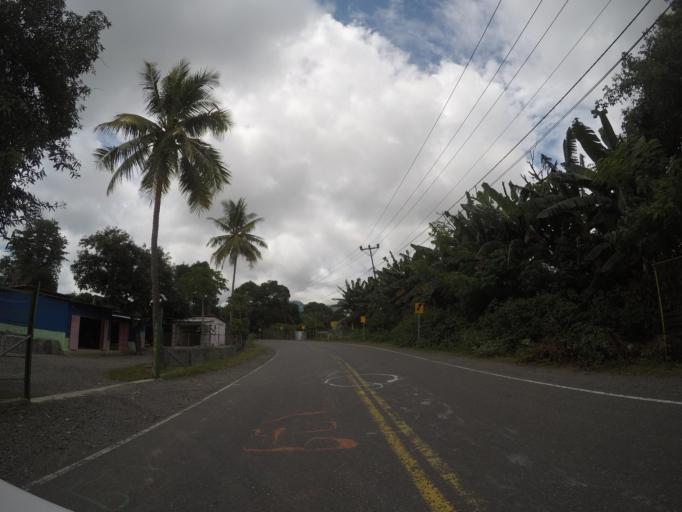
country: TL
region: Liquica
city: Maubara
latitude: -8.7321
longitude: 125.1360
